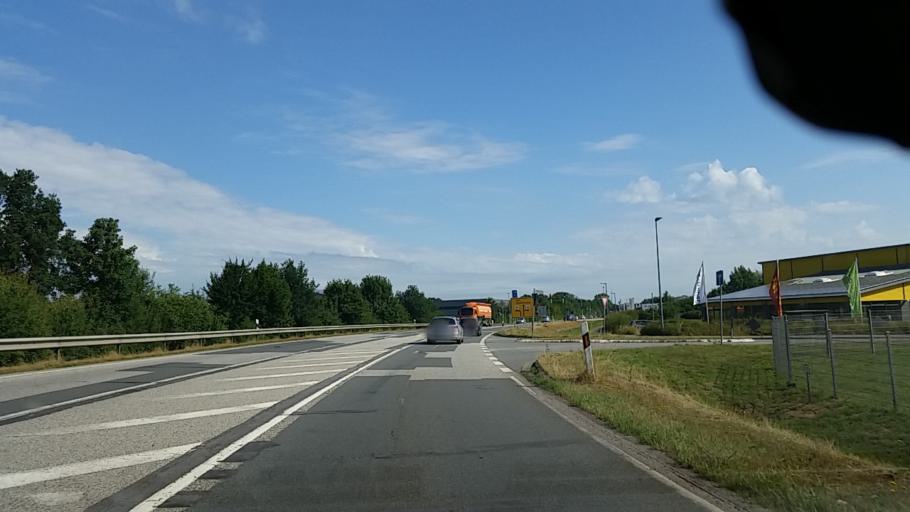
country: DE
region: Schleswig-Holstein
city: Kaltenkirchen
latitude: 53.8154
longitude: 9.9698
